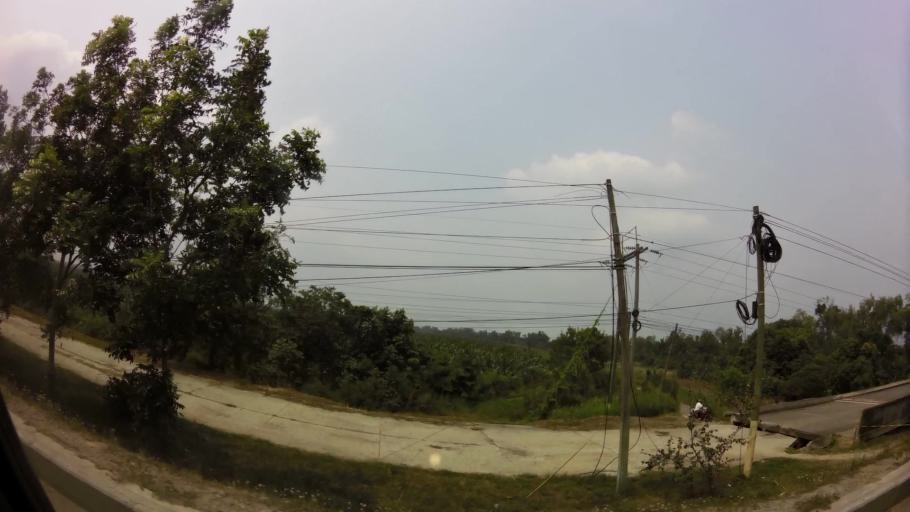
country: HN
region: Yoro
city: El Progreso
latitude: 15.4045
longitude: -87.8214
